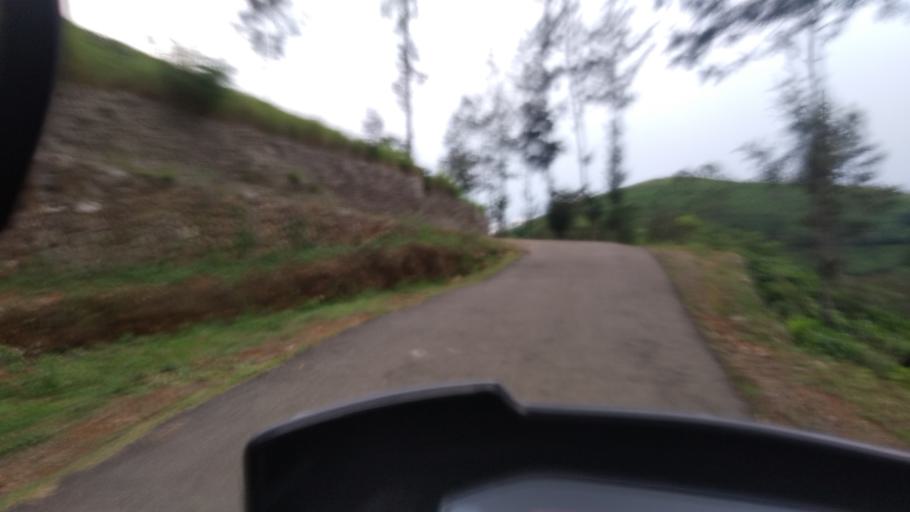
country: IN
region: Tamil Nadu
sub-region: Theni
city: Gudalur
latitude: 9.5429
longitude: 77.0472
